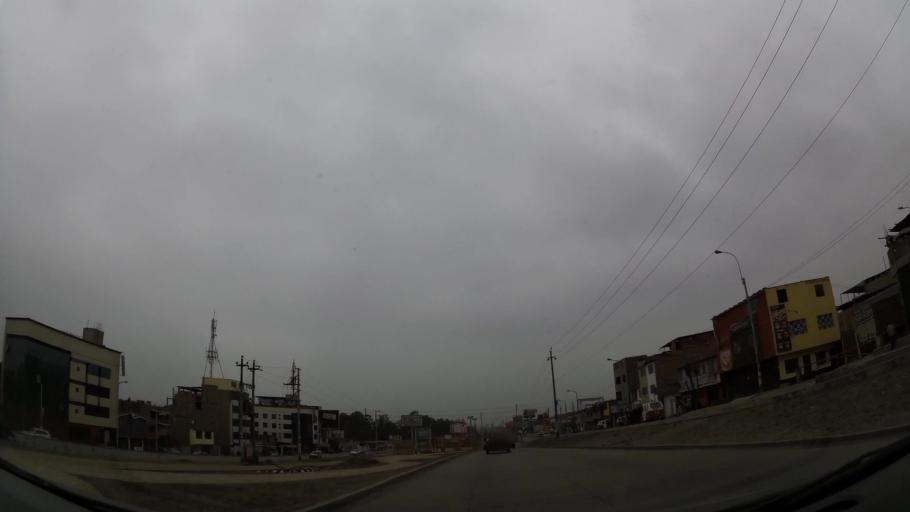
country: PE
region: Lima
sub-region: Lima
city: Surco
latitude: -12.2071
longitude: -76.9520
